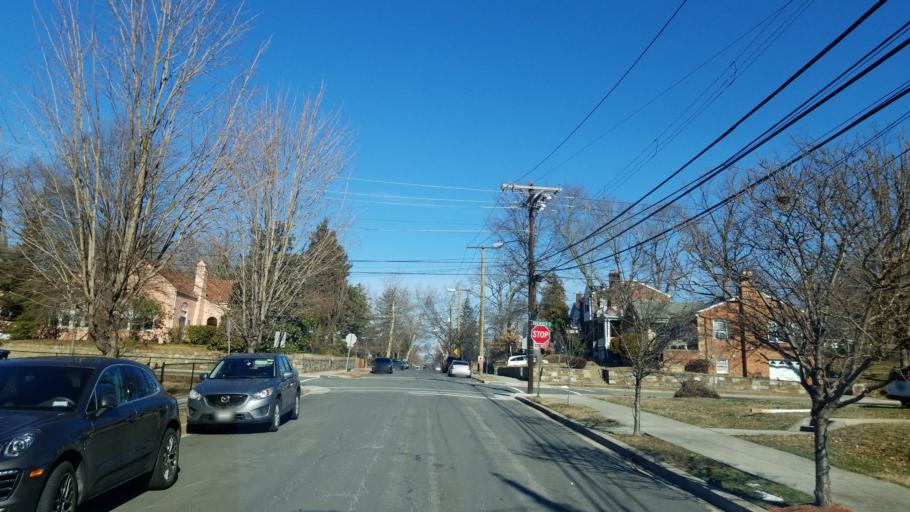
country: US
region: Maryland
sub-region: Prince George's County
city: Silver Hill
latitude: 38.8580
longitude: -76.9615
